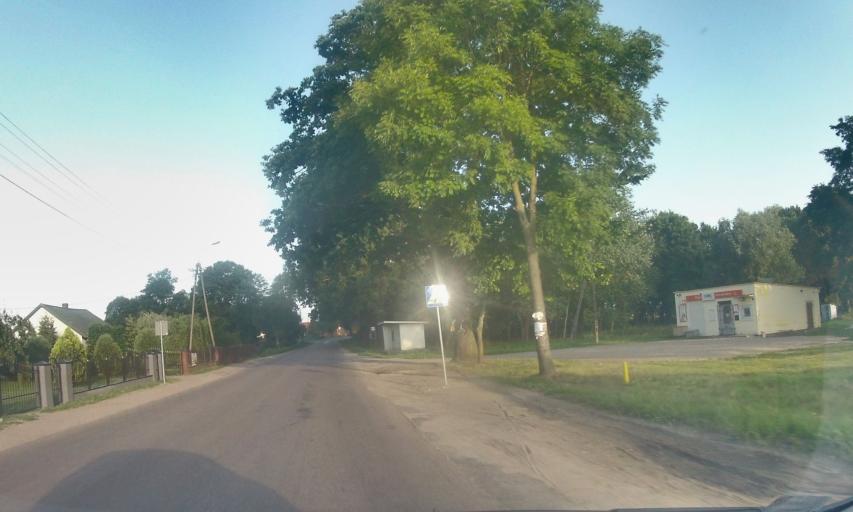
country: PL
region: Masovian Voivodeship
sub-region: Powiat mlawski
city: Szrensk
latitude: 52.9957
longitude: 20.2059
